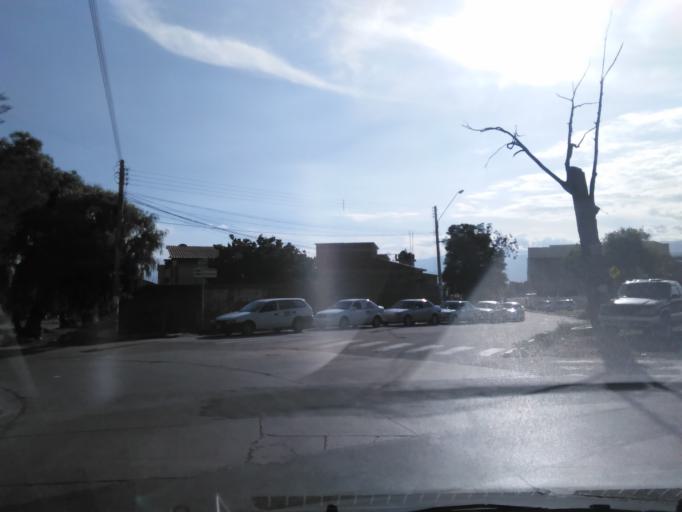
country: BO
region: Cochabamba
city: Cochabamba
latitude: -17.3503
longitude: -66.1845
